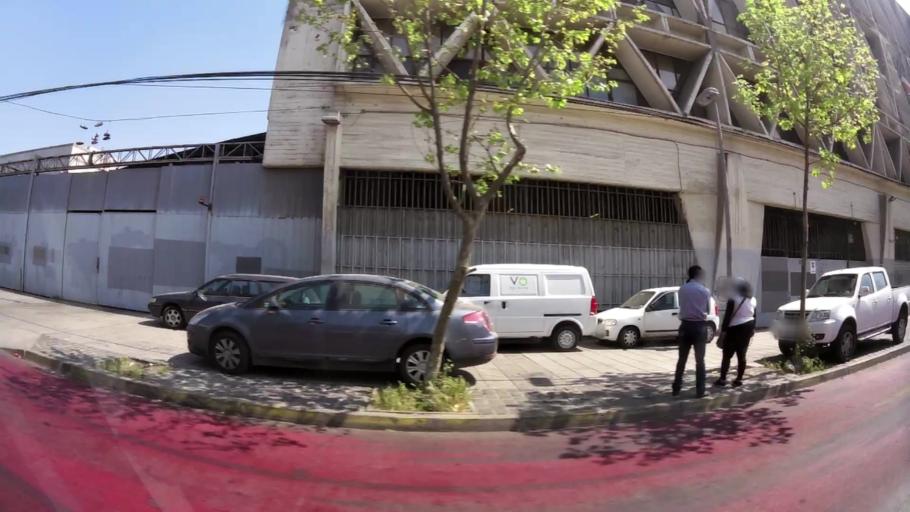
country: CL
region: Santiago Metropolitan
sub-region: Provincia de Santiago
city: Santiago
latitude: -33.4542
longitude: -70.6781
